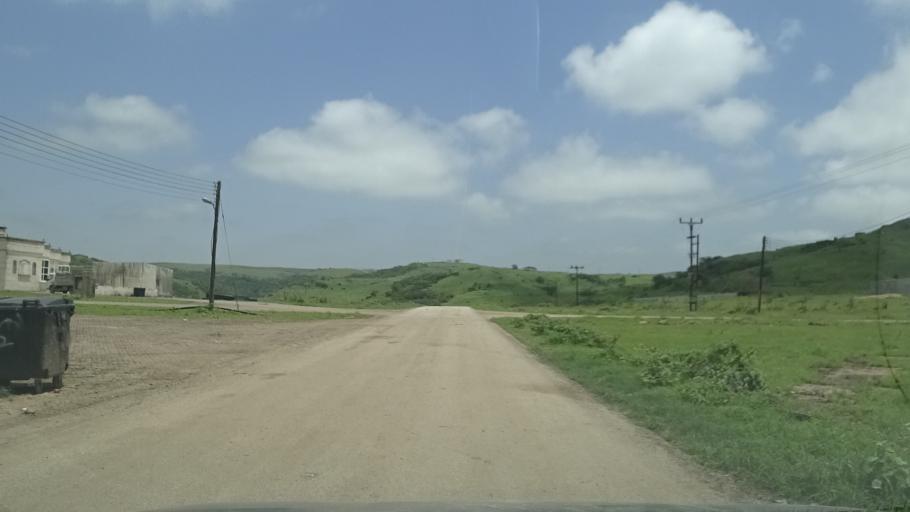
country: OM
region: Zufar
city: Salalah
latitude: 17.2125
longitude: 54.1923
